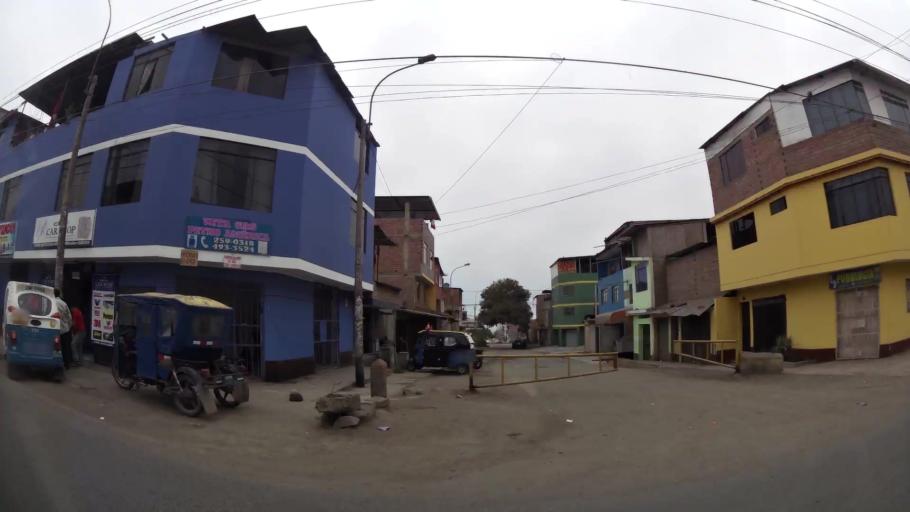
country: PE
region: Lima
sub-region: Lima
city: Surco
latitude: -12.2082
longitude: -76.9366
